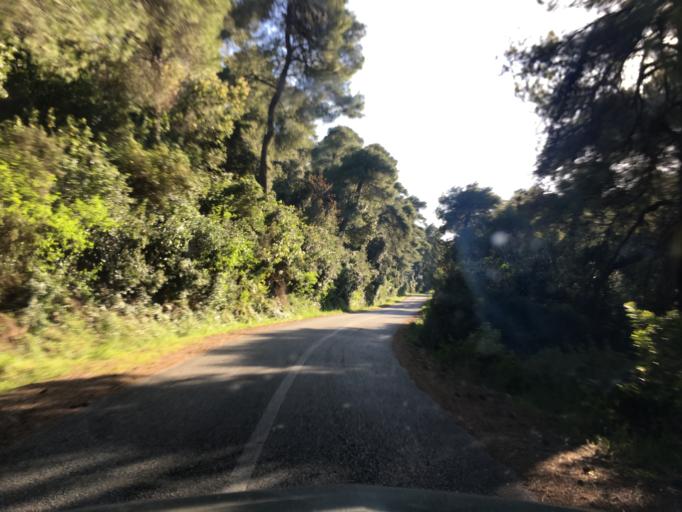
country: GR
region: Thessaly
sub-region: Nomos Magnisias
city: Skopelos
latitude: 39.1878
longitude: 23.6158
